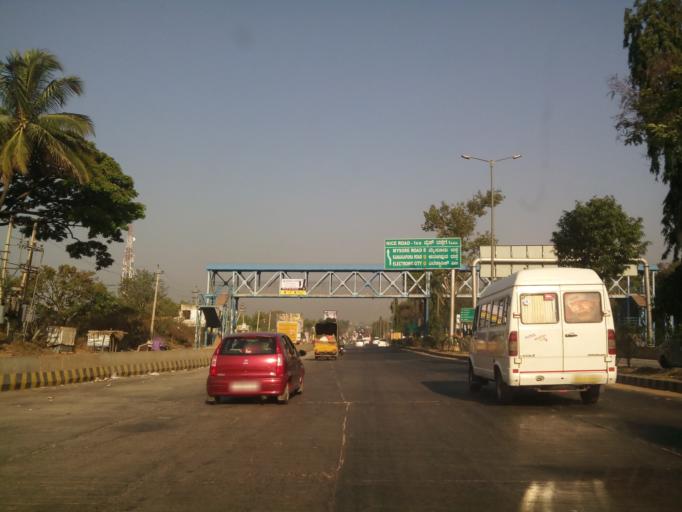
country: IN
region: Karnataka
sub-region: Bangalore Rural
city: Nelamangala
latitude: 13.0504
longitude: 77.4925
